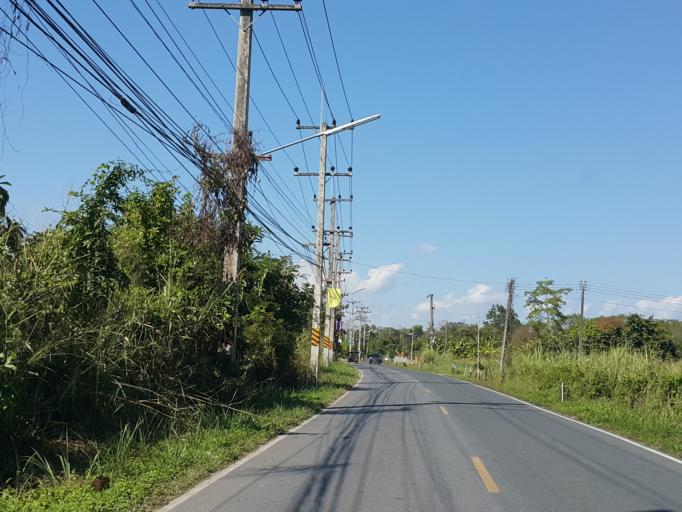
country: TH
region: Chiang Mai
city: San Sai
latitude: 18.9457
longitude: 98.9272
